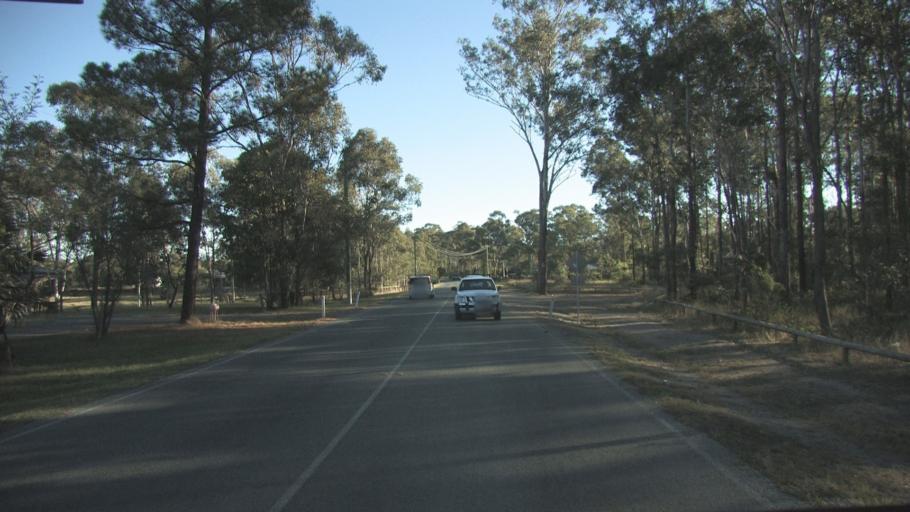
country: AU
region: Queensland
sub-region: Logan
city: Chambers Flat
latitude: -27.7460
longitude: 153.0617
